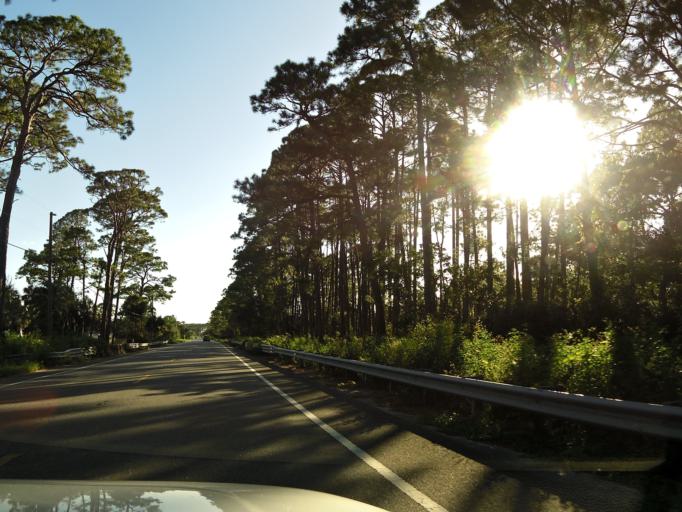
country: US
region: Florida
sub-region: Franklin County
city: Carrabelle
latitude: 29.7982
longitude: -84.7450
